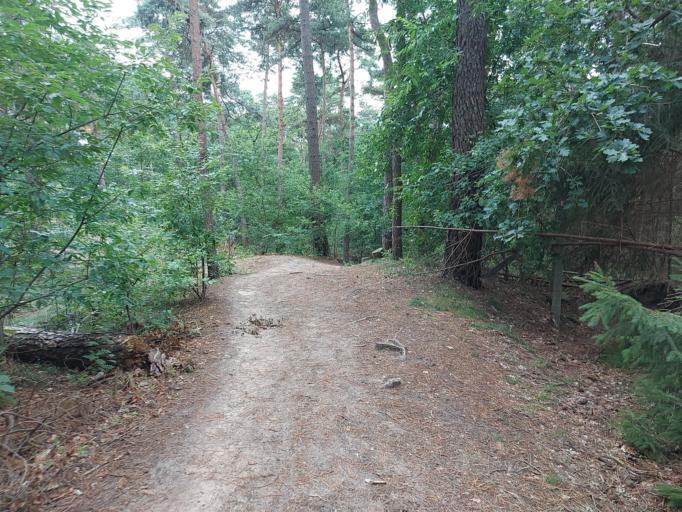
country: BE
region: Flanders
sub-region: Provincie Antwerpen
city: Meerhout
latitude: 51.1561
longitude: 5.0565
